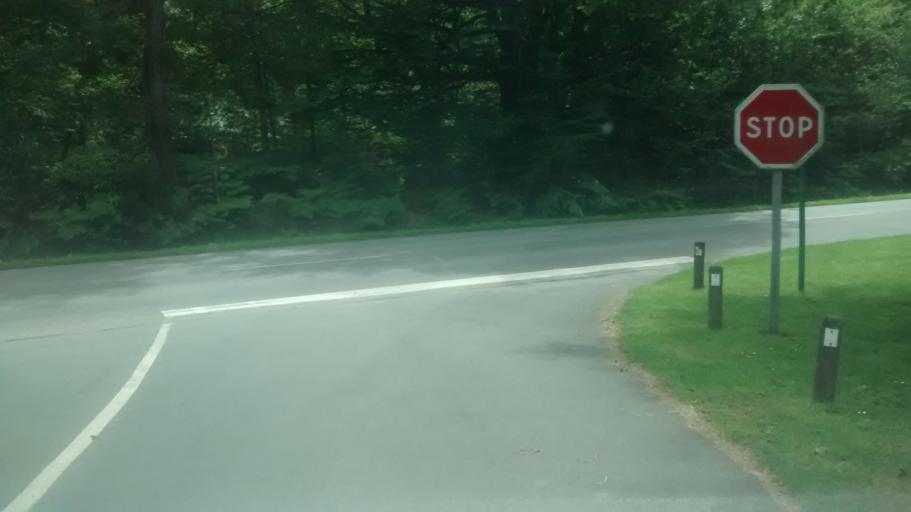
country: FR
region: Brittany
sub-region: Departement du Morbihan
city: Molac
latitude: 47.7798
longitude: -2.4353
